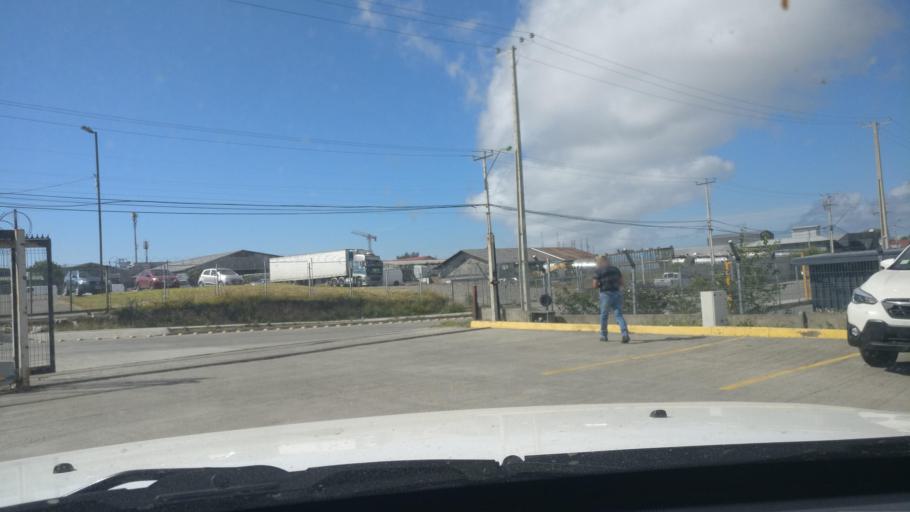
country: CL
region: Los Lagos
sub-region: Provincia de Llanquihue
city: Puerto Montt
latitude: -41.4530
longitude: -72.9636
